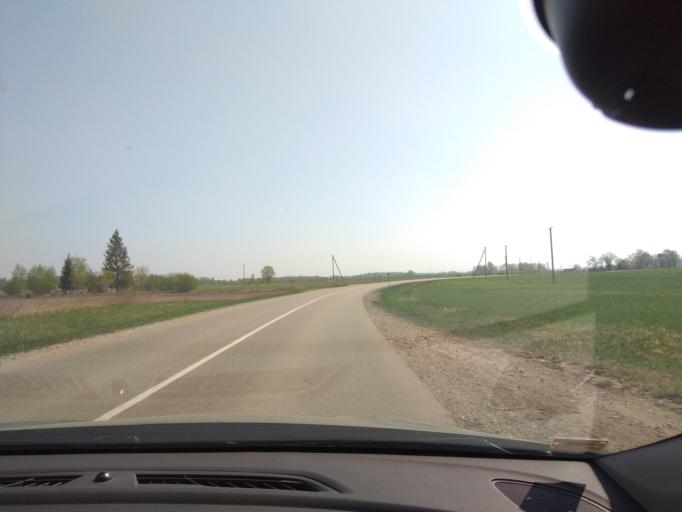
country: LT
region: Panevezys
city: Pasvalys
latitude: 55.9705
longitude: 24.2069
